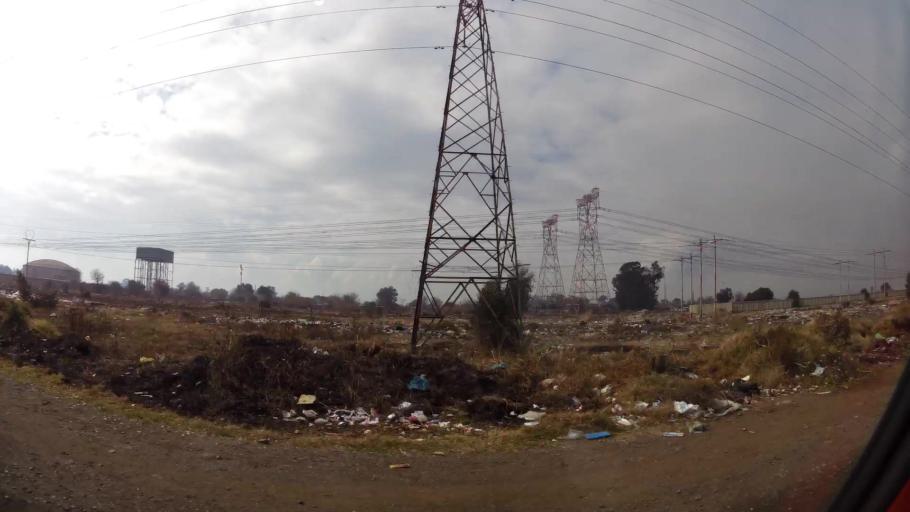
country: ZA
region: Gauteng
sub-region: Sedibeng District Municipality
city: Vanderbijlpark
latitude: -26.6902
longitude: 27.8607
